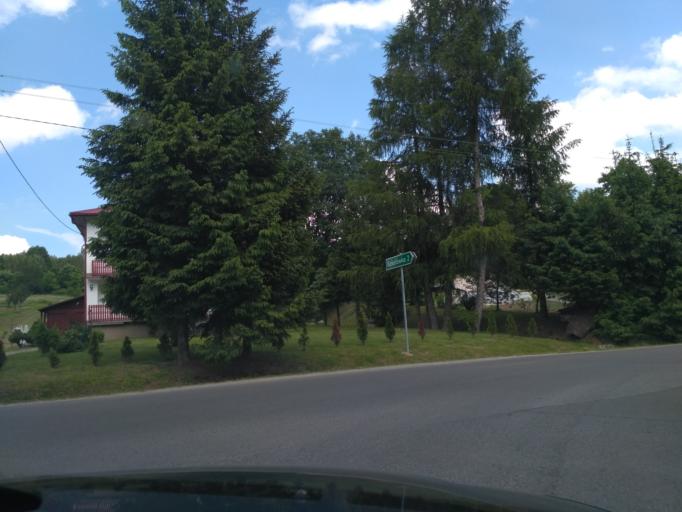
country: PL
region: Subcarpathian Voivodeship
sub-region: Powiat rzeszowski
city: Blazowa
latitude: 49.8740
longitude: 22.0671
